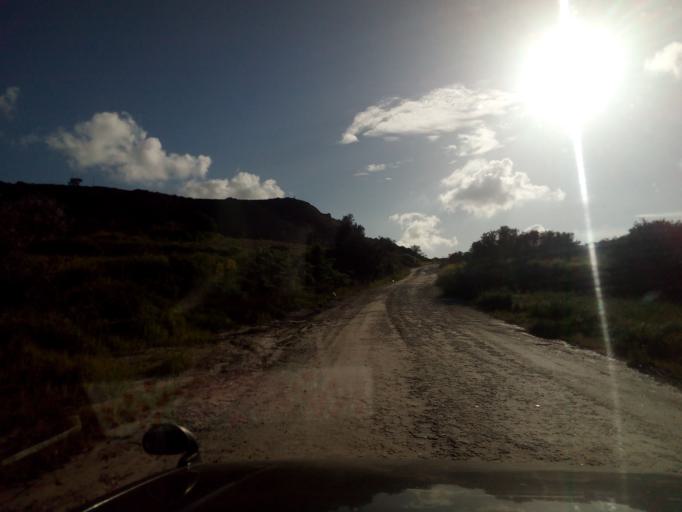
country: CY
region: Larnaka
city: Kofinou
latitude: 34.8057
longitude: 33.4309
